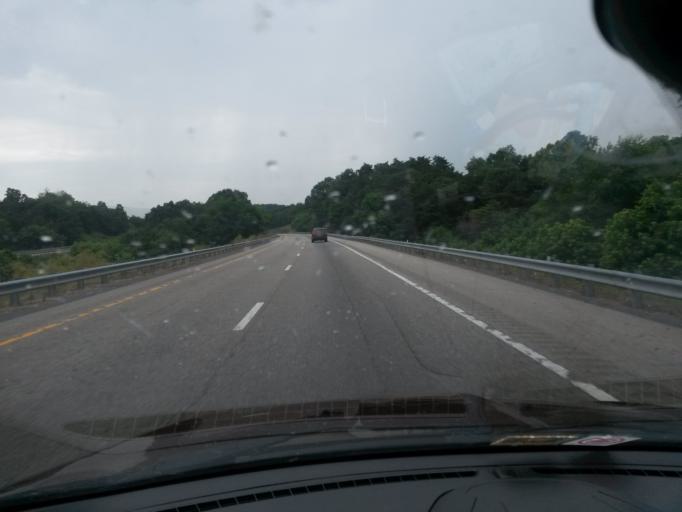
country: US
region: Virginia
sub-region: Rockbridge County
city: East Lexington
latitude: 37.8370
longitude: -79.4460
